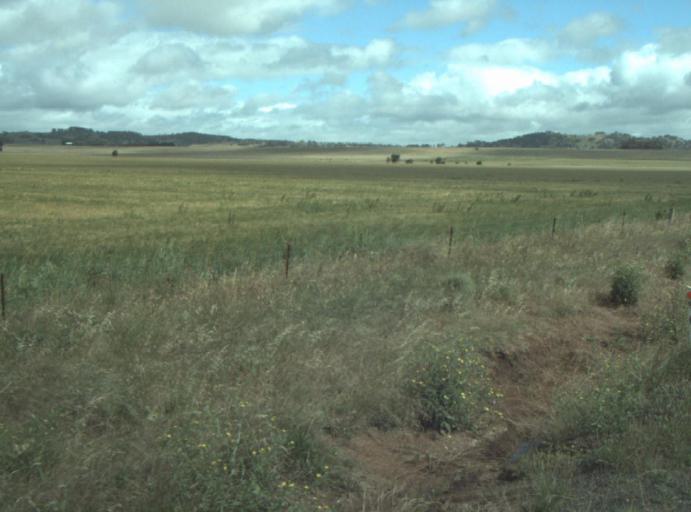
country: AU
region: Victoria
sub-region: Greater Geelong
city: Lara
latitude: -37.9063
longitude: 144.3164
